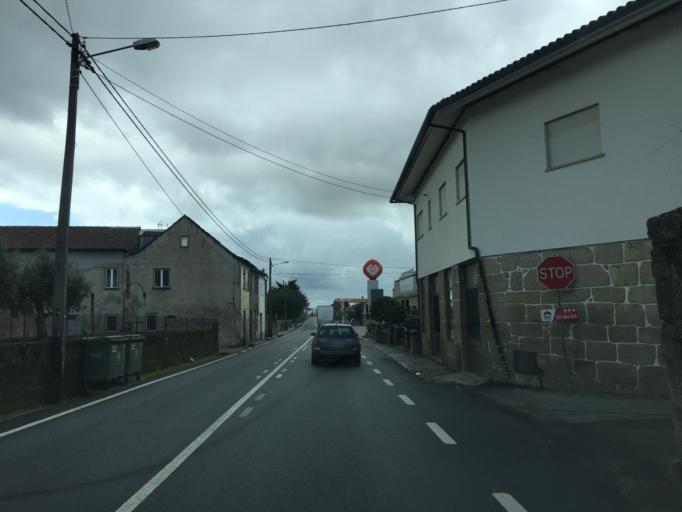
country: PT
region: Coimbra
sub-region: Oliveira do Hospital
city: Oliveira do Hospital
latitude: 40.3152
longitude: -7.8982
